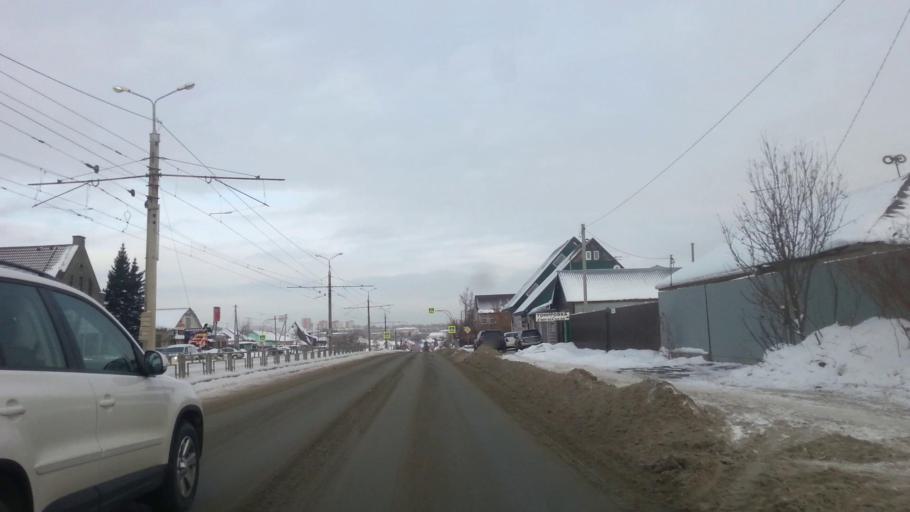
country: RU
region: Altai Krai
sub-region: Gorod Barnaulskiy
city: Barnaul
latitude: 53.3630
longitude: 83.7289
